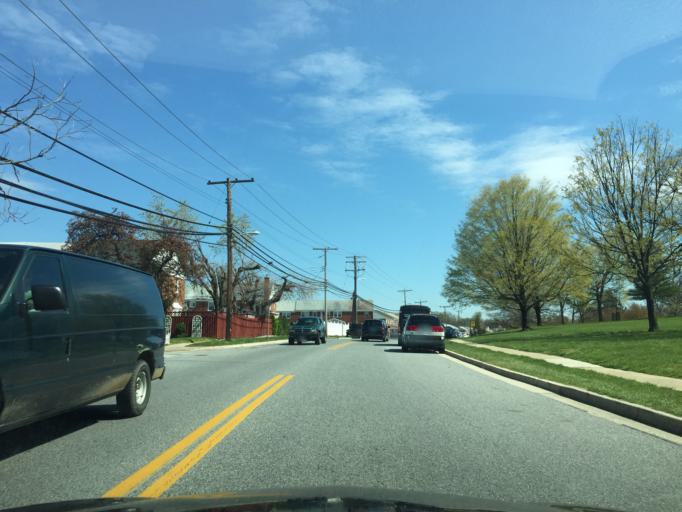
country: US
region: Maryland
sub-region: Baltimore County
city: Rossville
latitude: 39.3267
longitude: -76.4626
